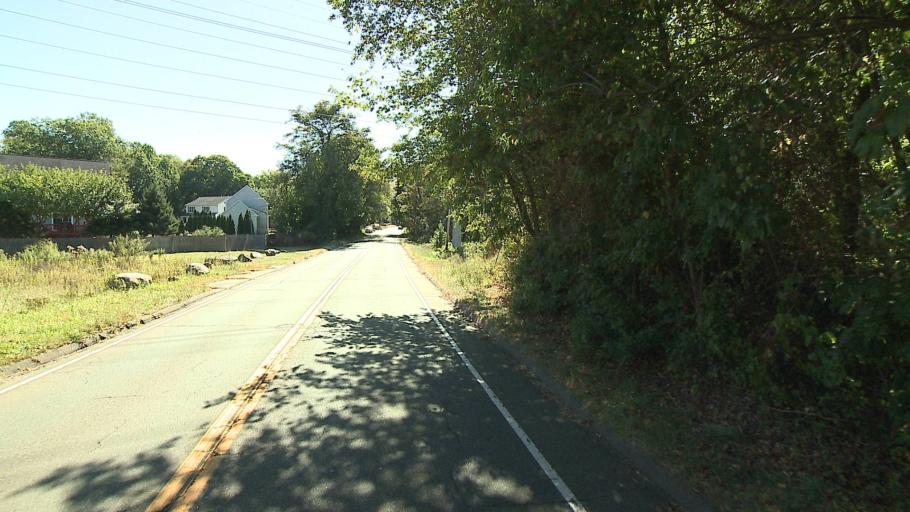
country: US
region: Connecticut
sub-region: New Haven County
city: Orange
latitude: 41.2560
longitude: -73.0503
